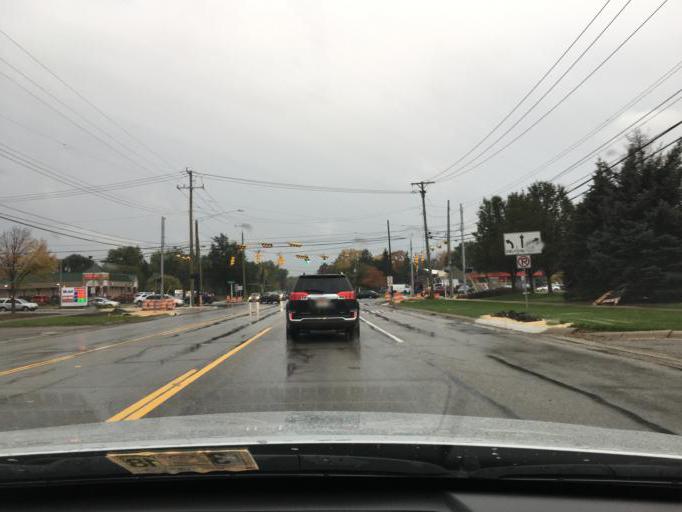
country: US
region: Michigan
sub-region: Oakland County
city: Rochester Hills
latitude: 42.6374
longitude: -83.1118
